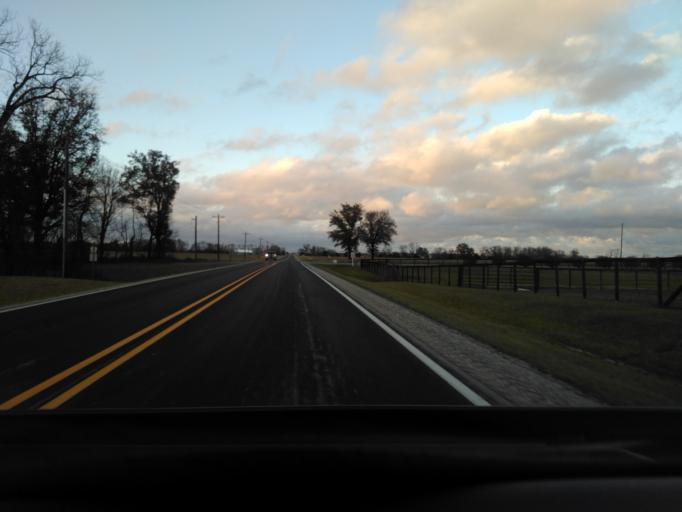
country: US
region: Illinois
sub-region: Effingham County
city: Altamont
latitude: 38.9854
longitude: -88.7488
